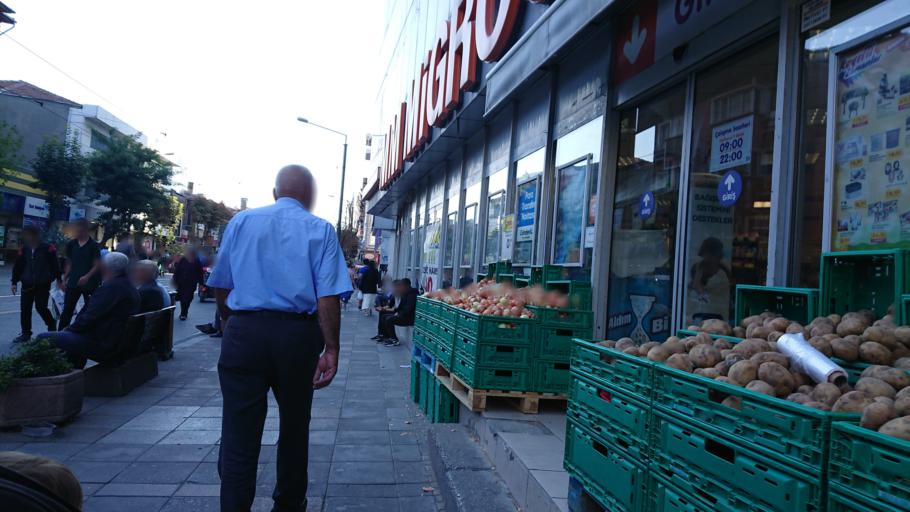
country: TR
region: Eskisehir
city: Eskisehir
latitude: 39.7746
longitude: 30.5176
